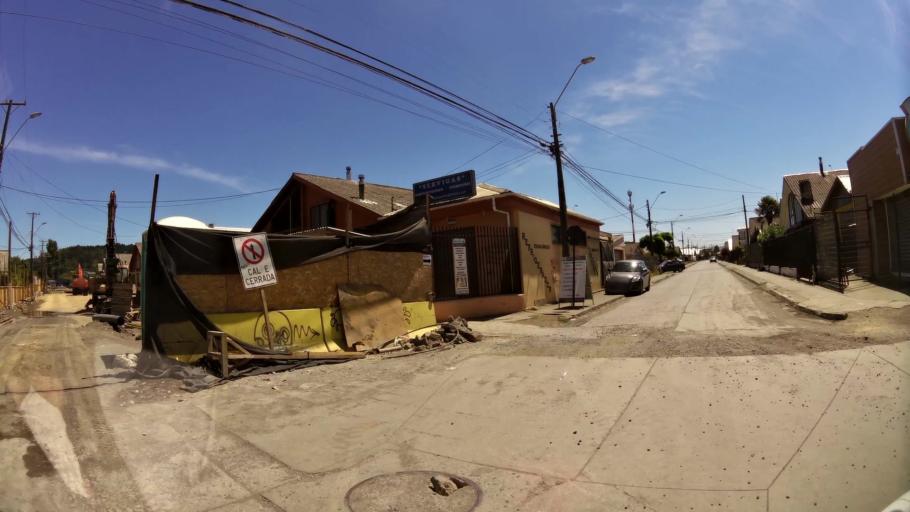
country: CL
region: Biobio
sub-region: Provincia de Concepcion
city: Talcahuano
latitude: -36.7529
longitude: -73.0905
